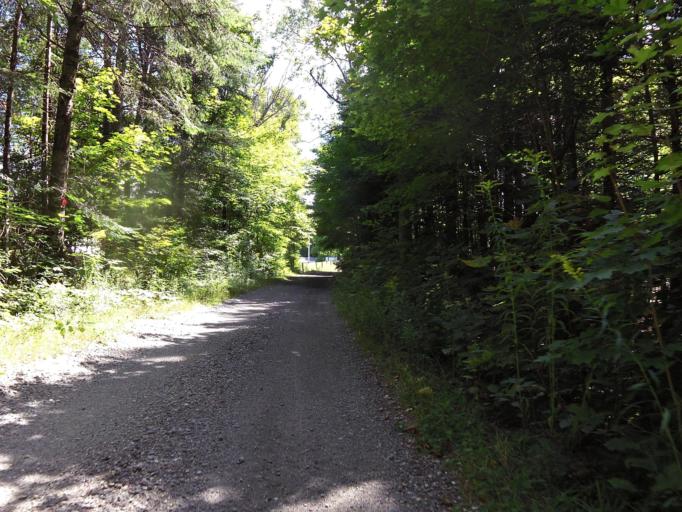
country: CA
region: Ontario
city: Renfrew
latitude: 45.0188
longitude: -76.7008
